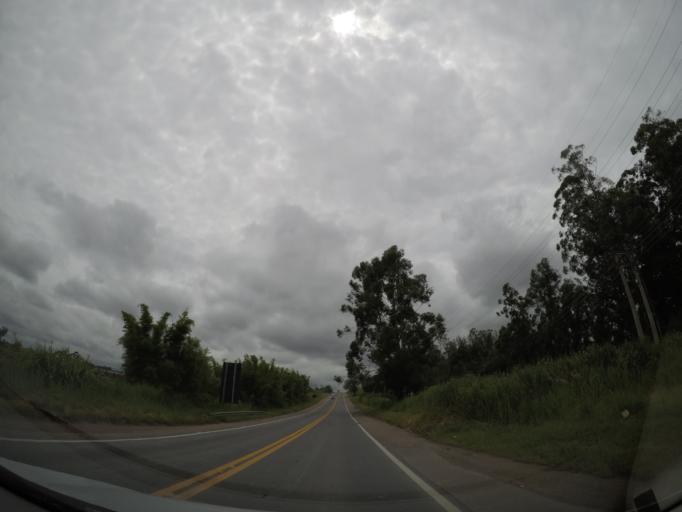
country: BR
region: Sao Paulo
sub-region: Vinhedo
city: Vinhedo
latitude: -23.0622
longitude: -47.0078
